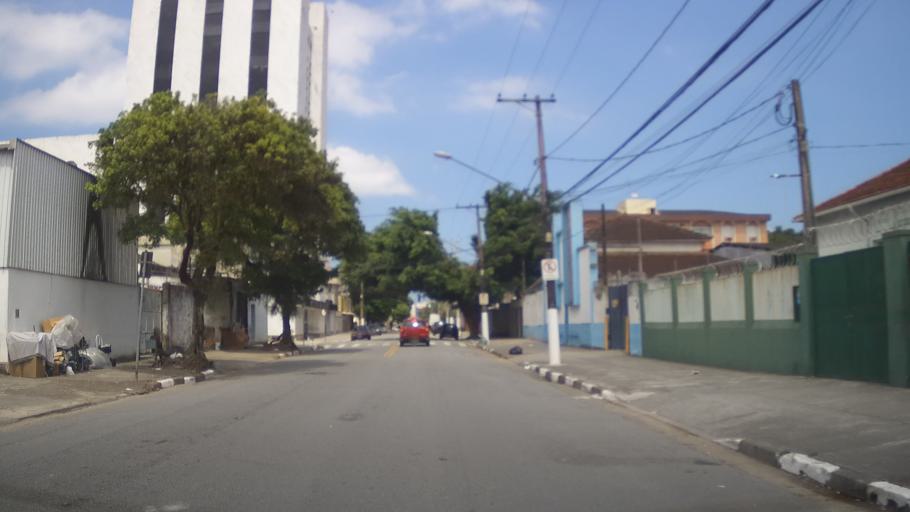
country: BR
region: Sao Paulo
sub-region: Santos
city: Santos
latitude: -23.9565
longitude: -46.3187
